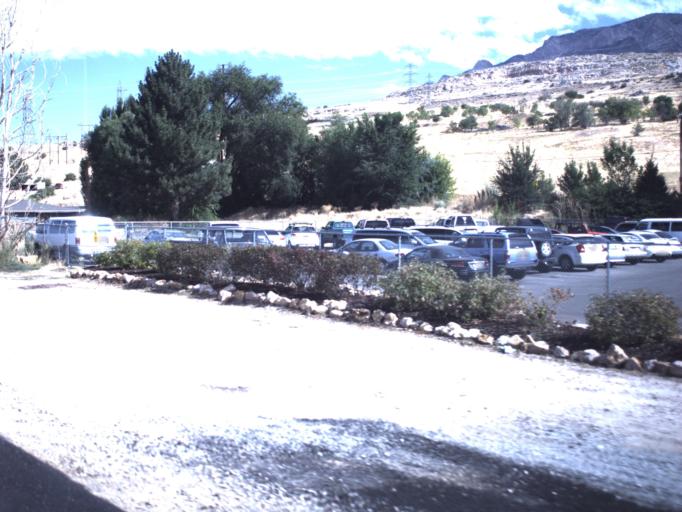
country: US
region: Utah
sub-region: Box Elder County
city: South Willard
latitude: 41.3328
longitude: -112.0253
